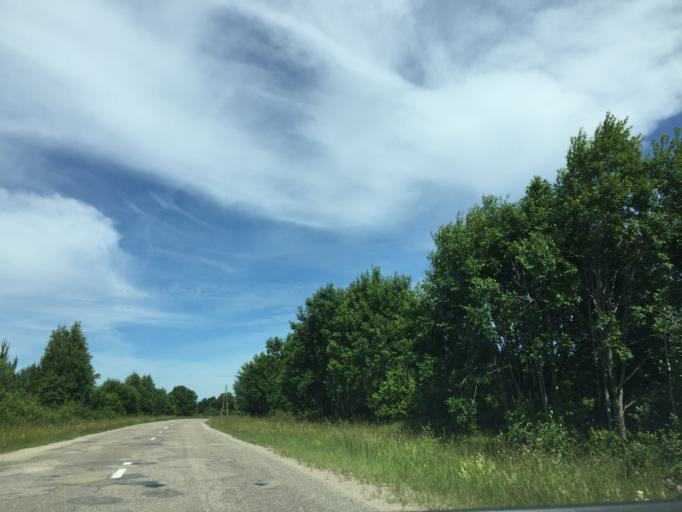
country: LV
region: Dundaga
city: Dundaga
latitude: 57.5452
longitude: 22.3236
